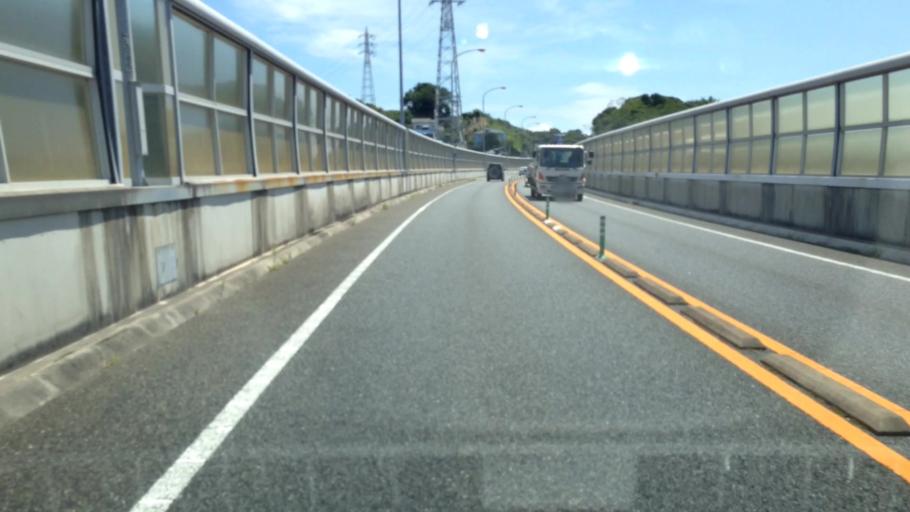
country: JP
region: Kanagawa
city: Yokosuka
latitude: 35.2180
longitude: 139.6375
